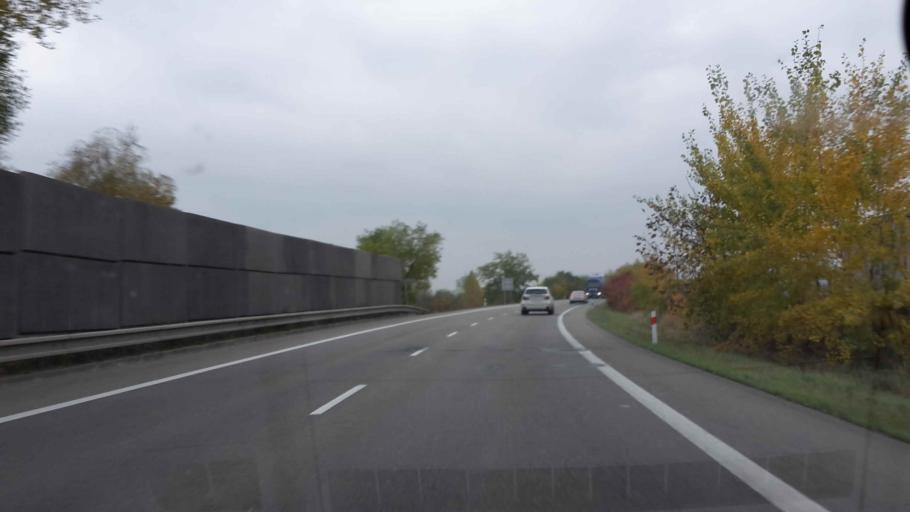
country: CZ
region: South Moravian
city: Slavkov u Brna
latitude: 49.1458
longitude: 16.8746
